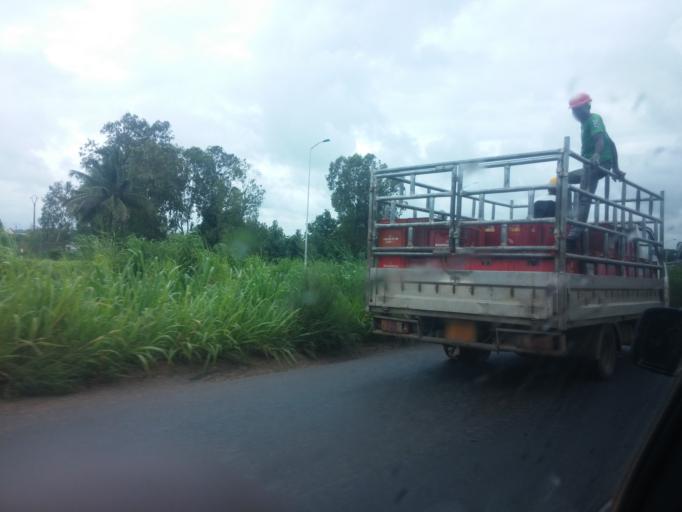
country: TG
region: Maritime
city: Tsevie
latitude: 6.3591
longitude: 1.2100
